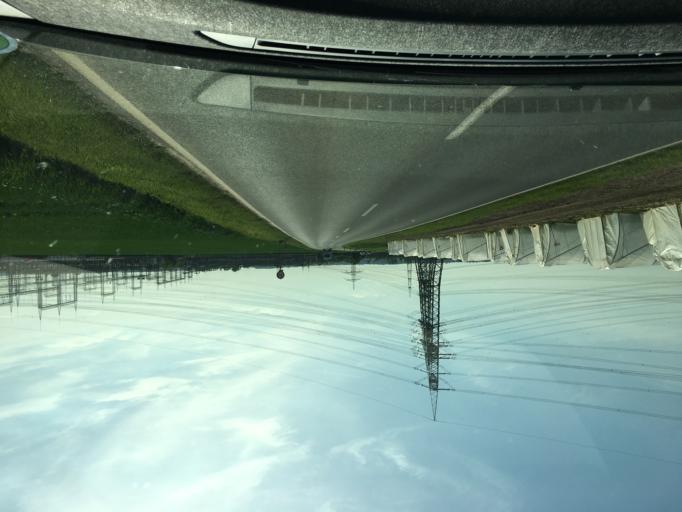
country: DE
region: North Rhine-Westphalia
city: Wesseling
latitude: 50.7970
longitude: 6.9787
